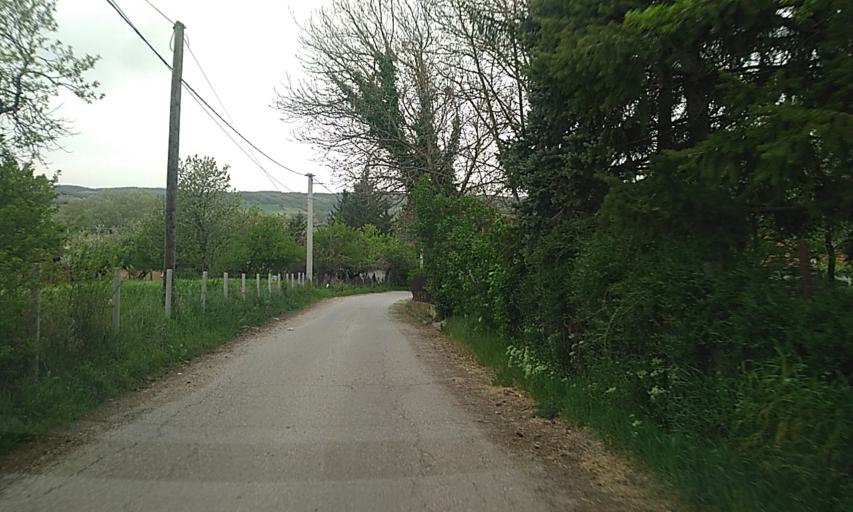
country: RS
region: Central Serbia
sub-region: Nisavski Okrug
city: Razanj
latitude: 43.5731
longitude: 21.5035
